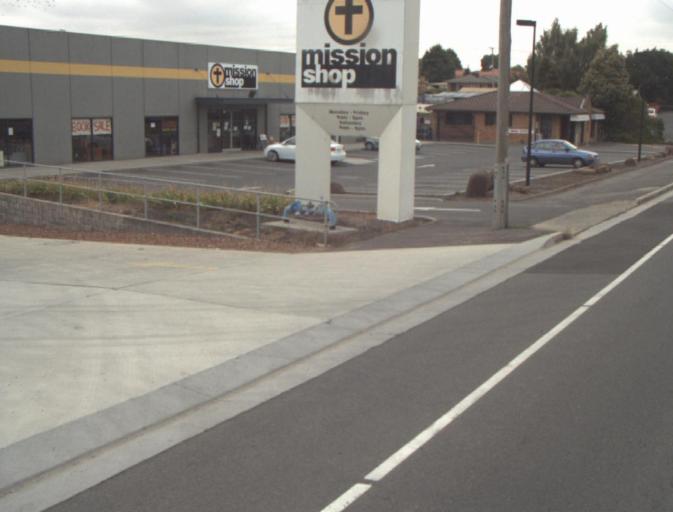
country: AU
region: Tasmania
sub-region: Launceston
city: Summerhill
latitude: -41.4837
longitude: 147.1676
